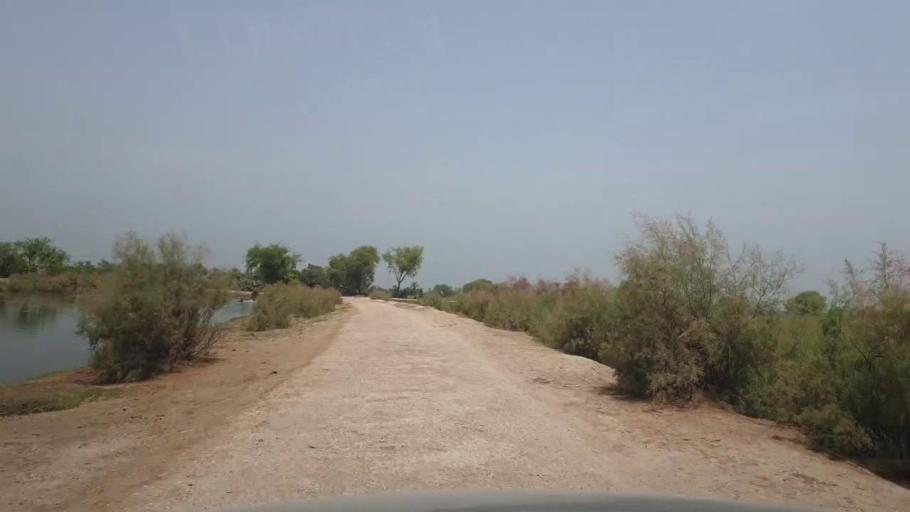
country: PK
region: Sindh
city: Garhi Yasin
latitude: 27.9212
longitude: 68.3755
